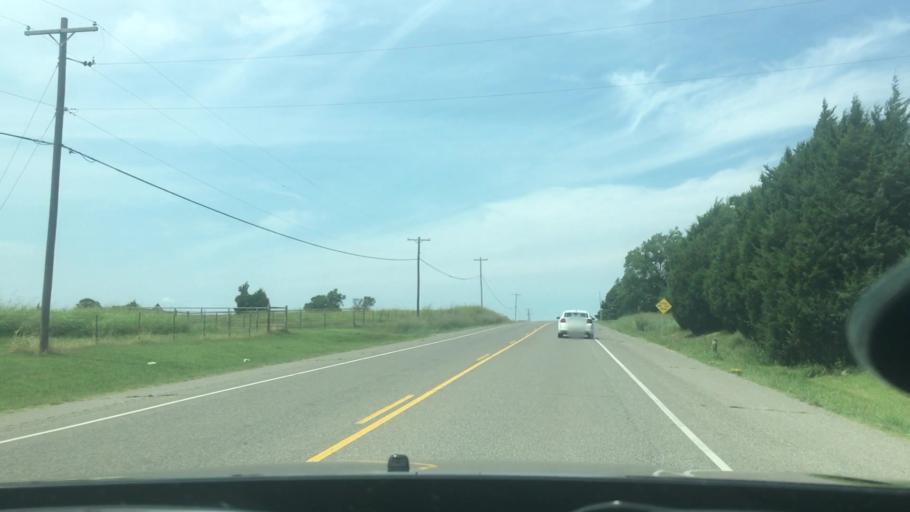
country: US
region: Oklahoma
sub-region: Pottawatomie County
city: Shawnee
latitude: 35.3331
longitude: -96.8185
